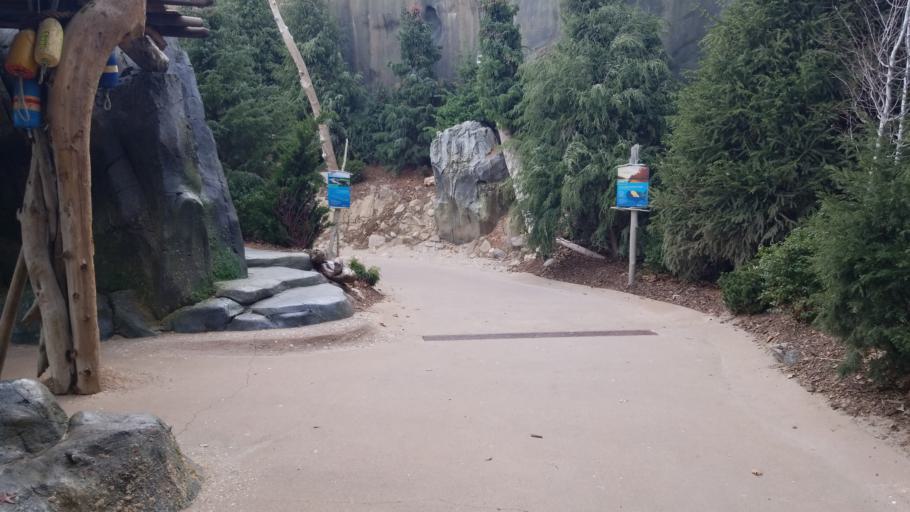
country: US
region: Nebraska
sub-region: Douglas County
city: Omaha
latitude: 41.2275
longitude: -95.9275
